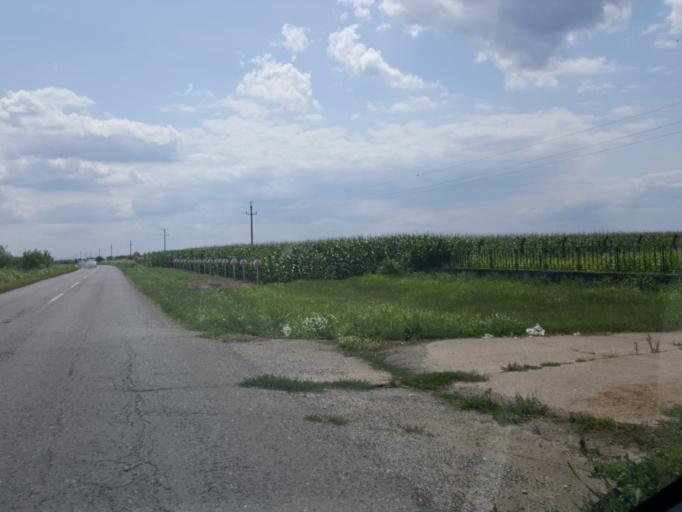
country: RS
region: Autonomna Pokrajina Vojvodina
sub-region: Sremski Okrug
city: Pecinci
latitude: 44.8841
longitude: 19.9608
